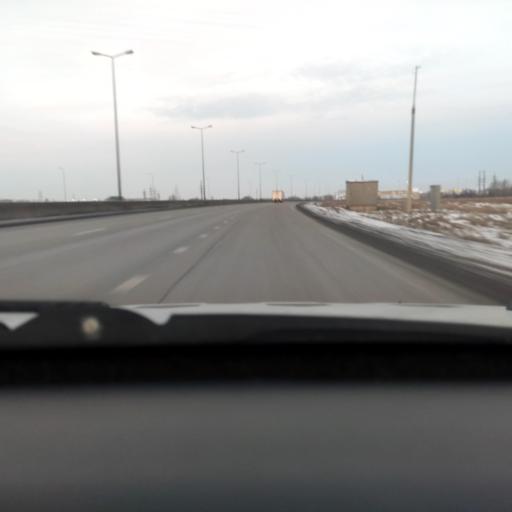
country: RU
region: Perm
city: Kondratovo
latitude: 57.9304
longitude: 56.1703
